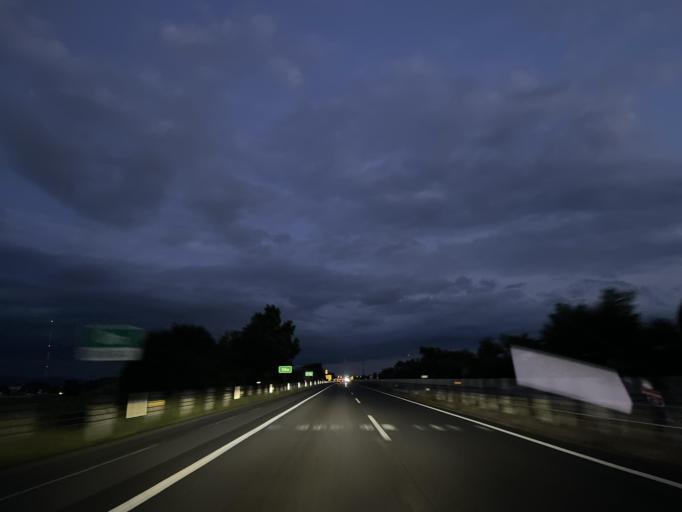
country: JP
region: Iwate
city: Morioka-shi
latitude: 39.6371
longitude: 141.1274
